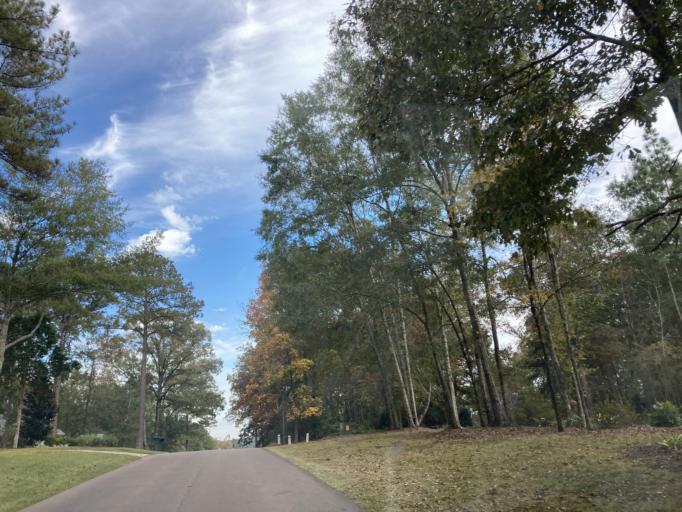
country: US
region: Mississippi
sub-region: Lamar County
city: West Hattiesburg
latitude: 31.3236
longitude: -89.4664
